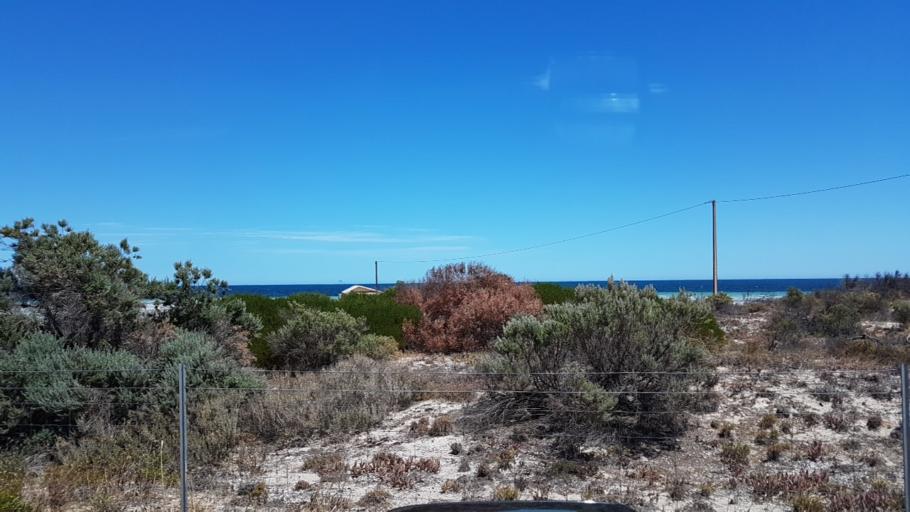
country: AU
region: South Australia
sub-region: Copper Coast
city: Wallaroo
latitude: -33.9010
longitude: 137.6289
